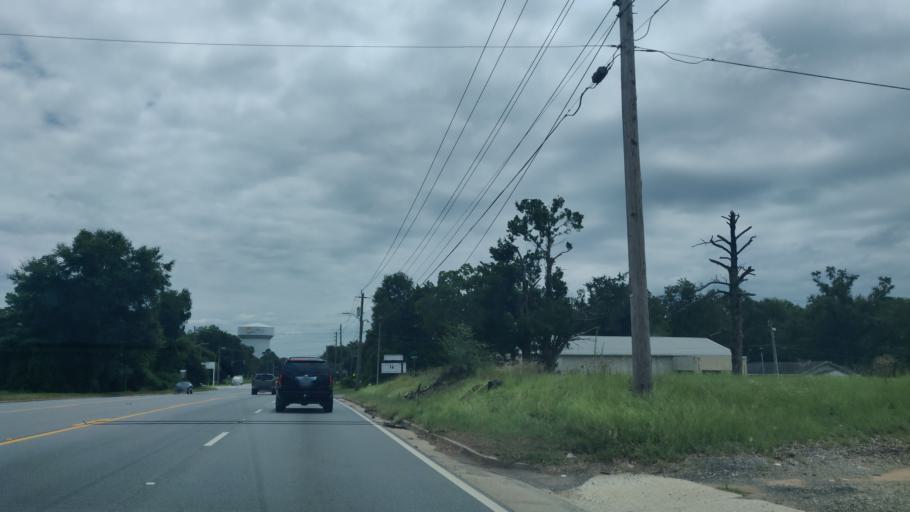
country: US
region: Georgia
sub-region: Dougherty County
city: Albany
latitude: 31.5798
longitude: -84.1072
